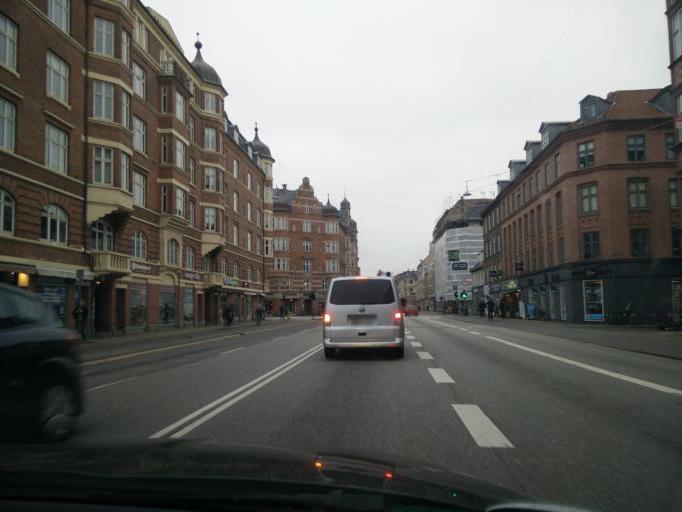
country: DK
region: Capital Region
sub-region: Kobenhavn
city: Christianshavn
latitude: 55.6646
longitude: 12.6002
